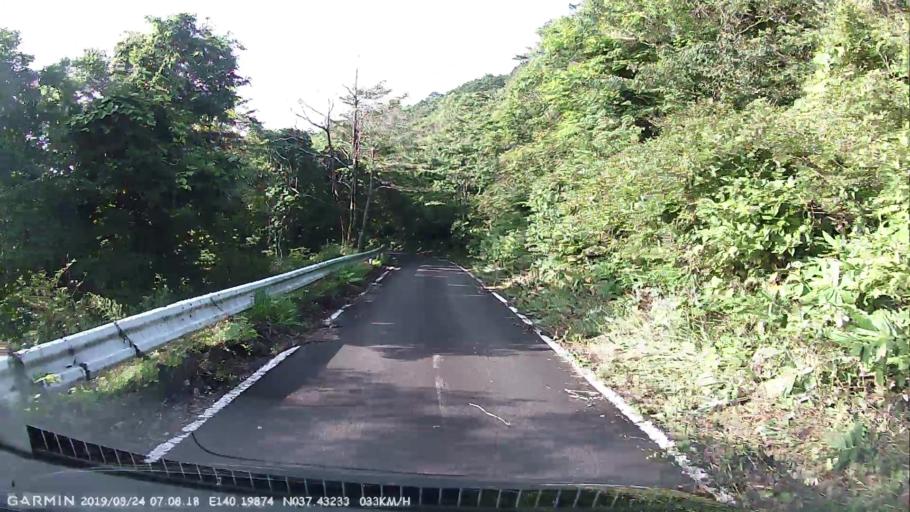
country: JP
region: Fukushima
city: Inawashiro
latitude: 37.4323
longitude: 140.1987
